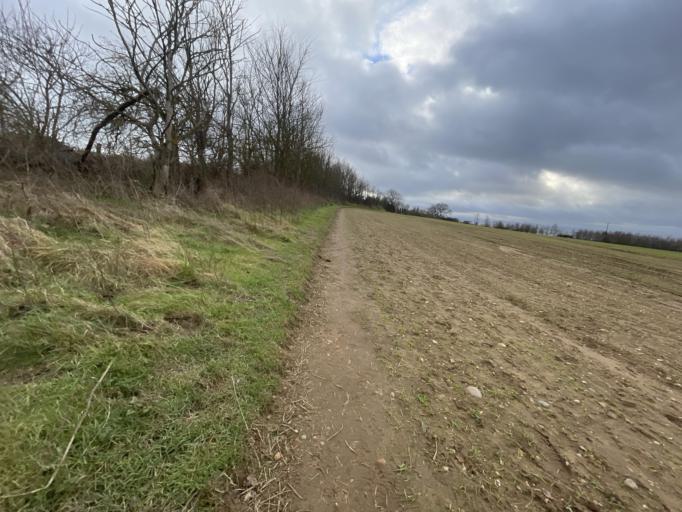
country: GB
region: England
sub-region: West Berkshire
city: Theale
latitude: 51.4463
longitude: -1.0665
